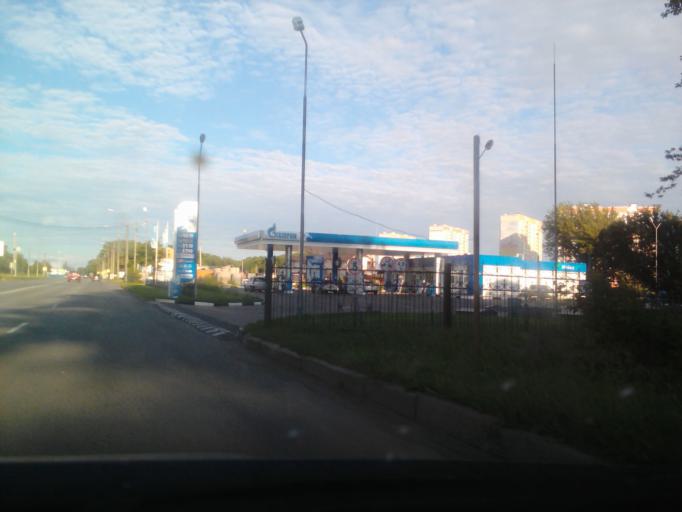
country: RU
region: Kursk
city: Kurchatov
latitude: 51.6585
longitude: 35.6463
